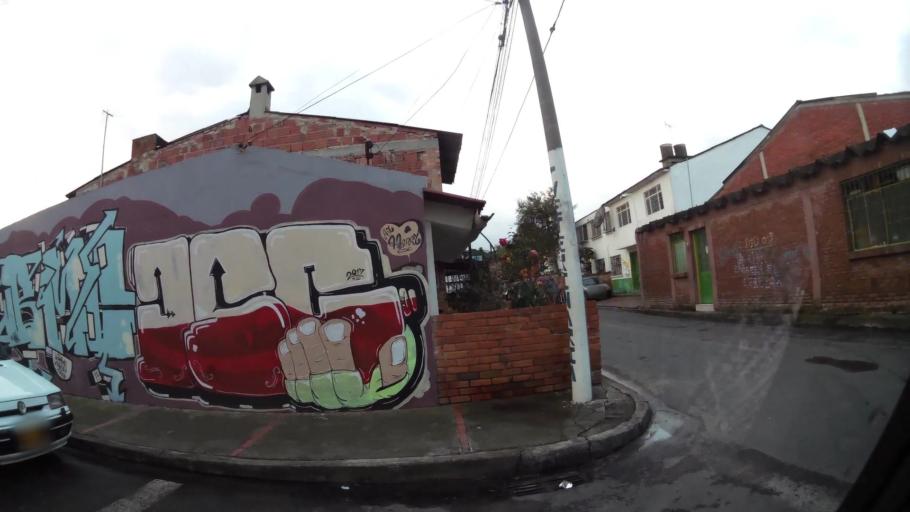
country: CO
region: Cundinamarca
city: Chia
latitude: 4.8563
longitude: -74.0565
